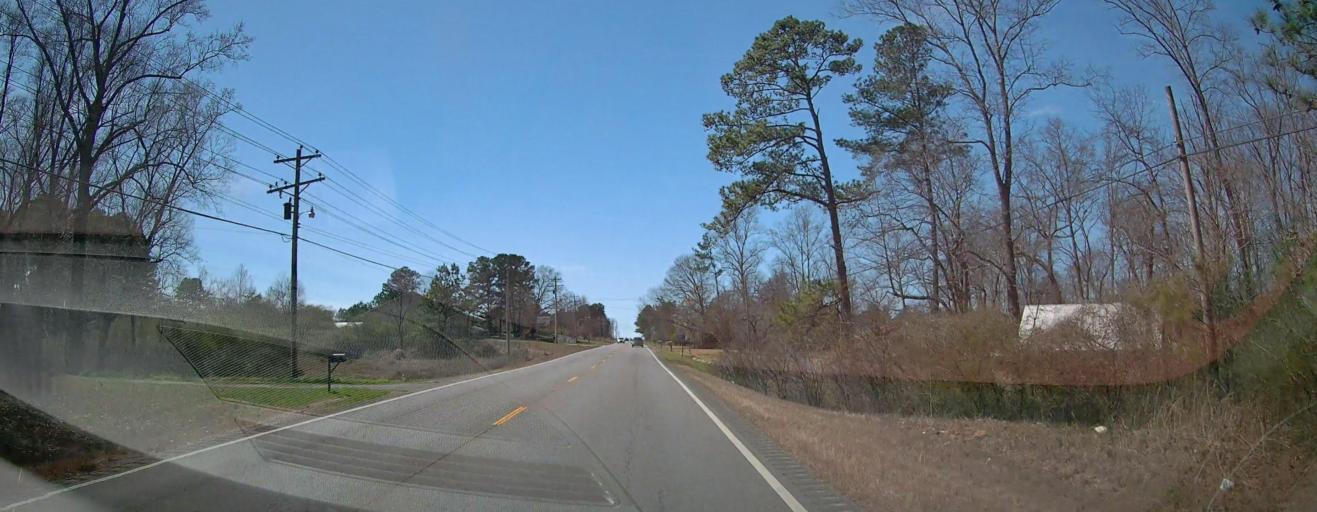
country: US
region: Alabama
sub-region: Blount County
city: Blountsville
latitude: 34.1746
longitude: -86.6307
